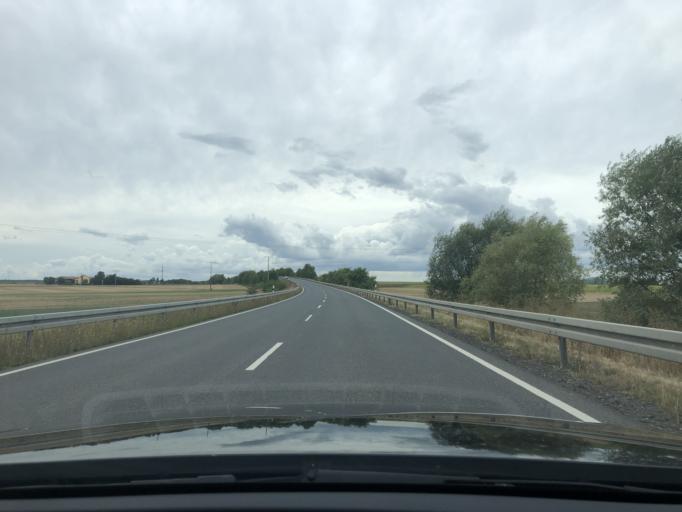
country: DE
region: Bavaria
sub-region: Regierungsbezirk Unterfranken
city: Hofheim in Unterfranken
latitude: 50.1273
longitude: 10.5337
